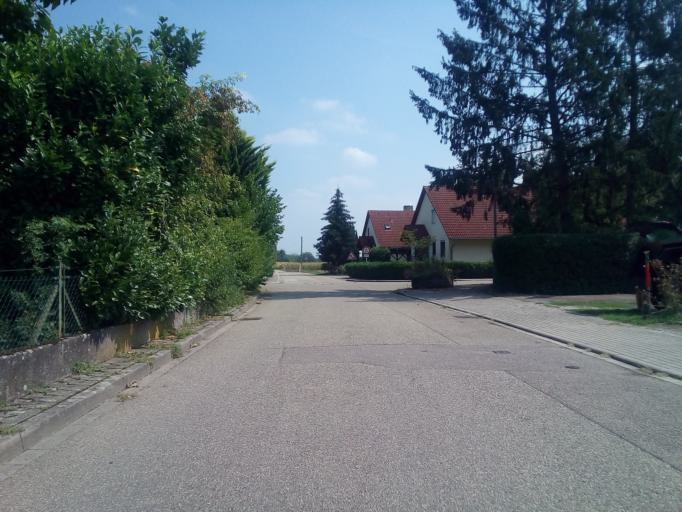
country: DE
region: Baden-Wuerttemberg
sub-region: Freiburg Region
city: Kehl
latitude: 48.6033
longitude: 7.8421
